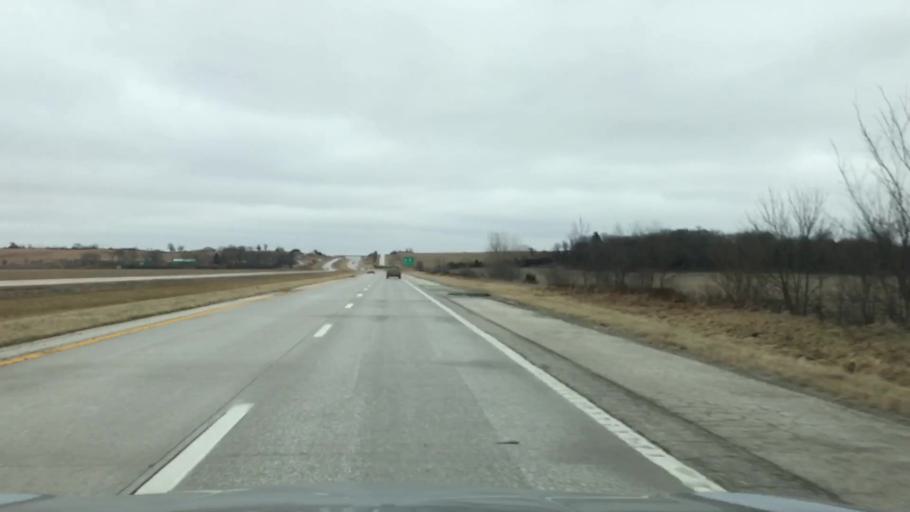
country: US
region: Missouri
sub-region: Linn County
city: Marceline
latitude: 39.7609
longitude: -92.9697
